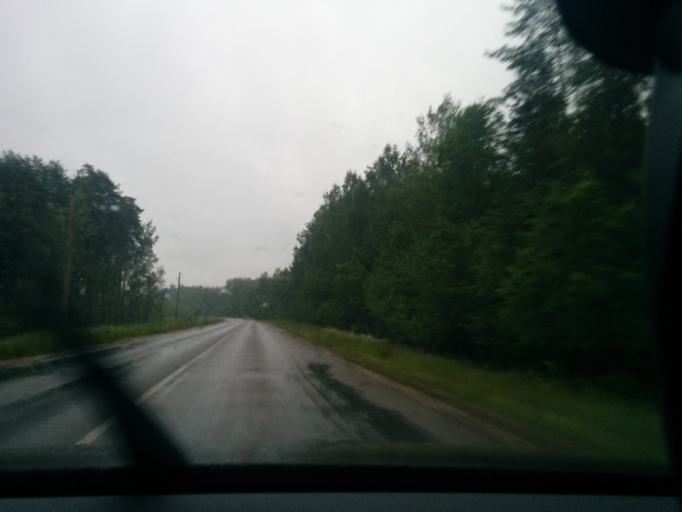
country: LV
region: Stopini
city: Ulbroka
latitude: 56.9150
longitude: 24.3276
